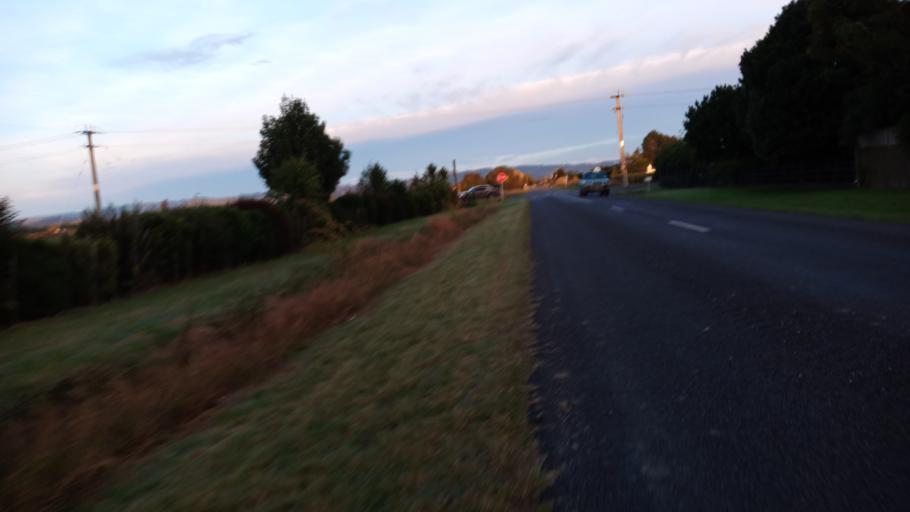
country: NZ
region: Gisborne
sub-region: Gisborne District
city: Gisborne
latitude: -38.6340
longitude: 177.9741
